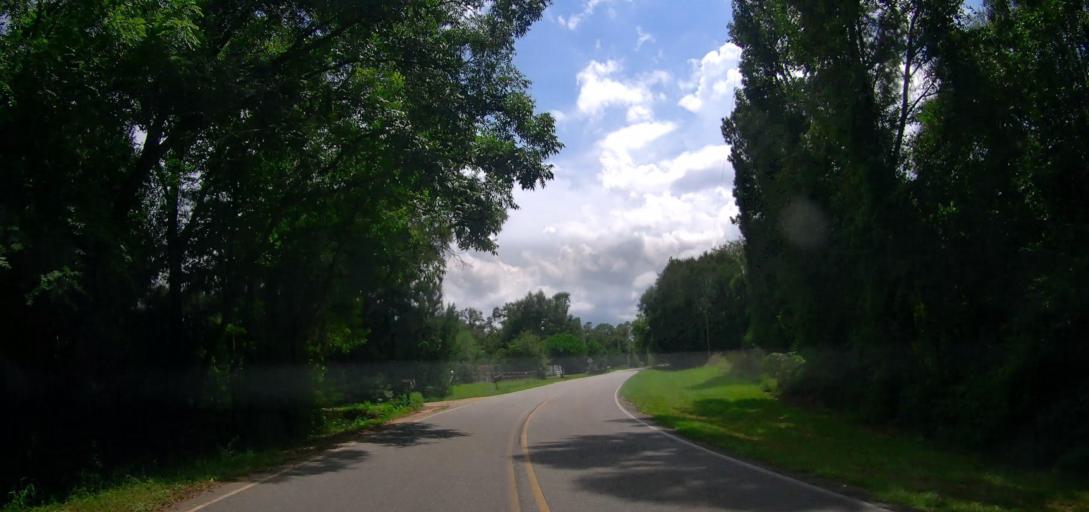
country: US
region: Georgia
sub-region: Houston County
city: Perry
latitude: 32.5216
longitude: -83.7466
